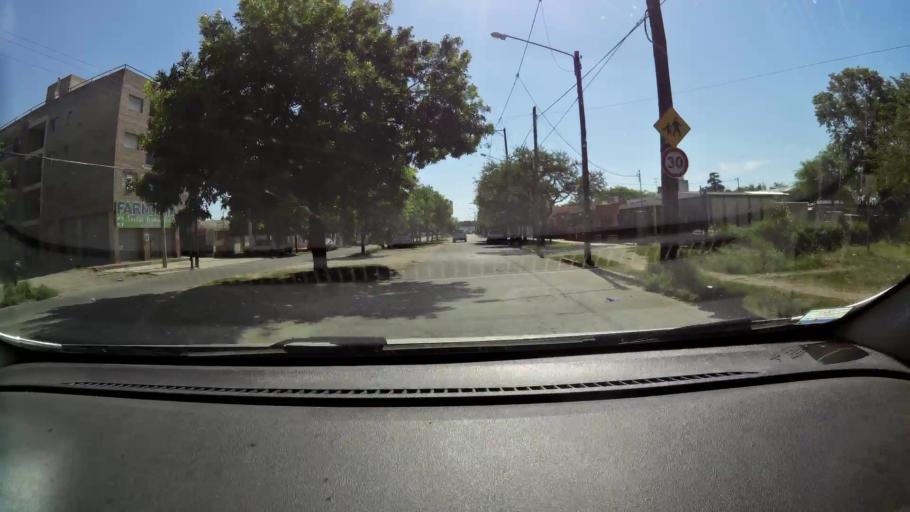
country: AR
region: Cordoba
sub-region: Departamento de Capital
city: Cordoba
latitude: -31.3680
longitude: -64.1738
